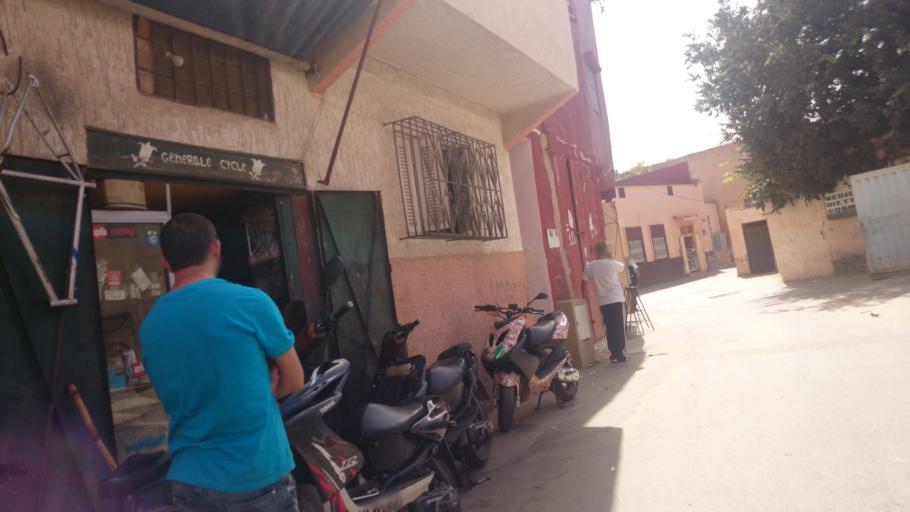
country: MA
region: Meknes-Tafilalet
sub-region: Meknes
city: Meknes
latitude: 33.8907
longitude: -5.5617
